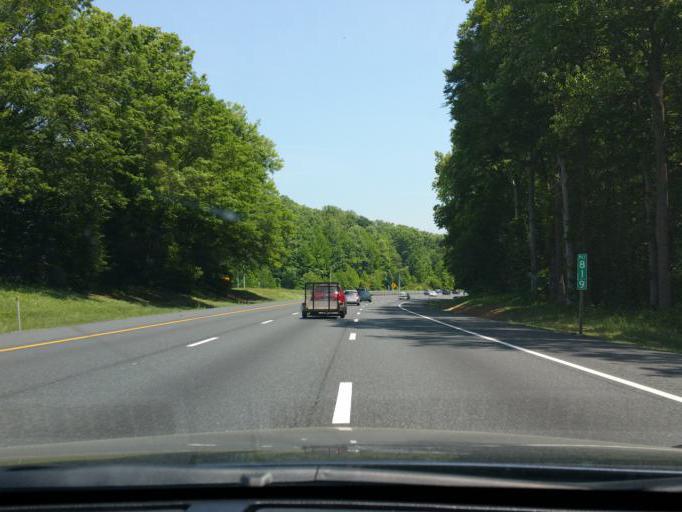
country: US
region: Maryland
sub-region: Harford County
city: Riverside
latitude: 39.4994
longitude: -76.2278
